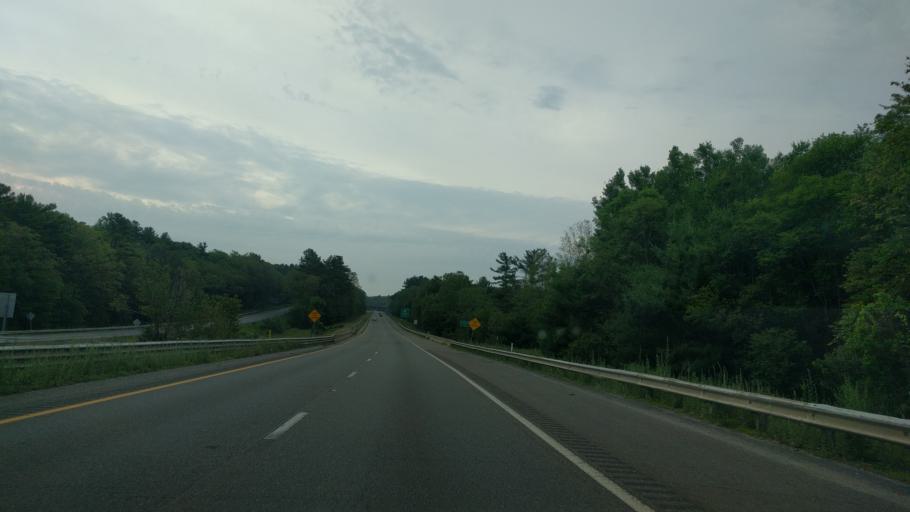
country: US
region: Massachusetts
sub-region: Worcester County
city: East Douglas
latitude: 42.0834
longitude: -71.6908
